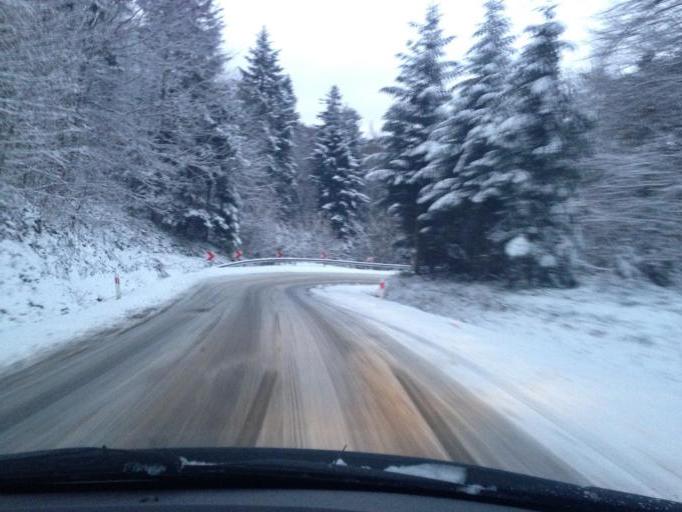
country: PL
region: Subcarpathian Voivodeship
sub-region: Powiat jasielski
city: Krempna
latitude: 49.5315
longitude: 21.5008
